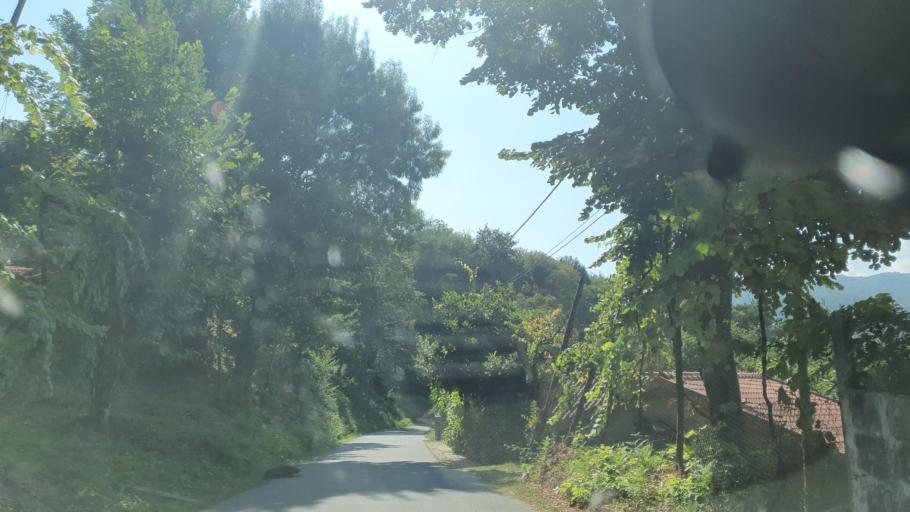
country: PT
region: Braga
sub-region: Vieira do Minho
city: Real
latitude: 41.6702
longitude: -8.1726
